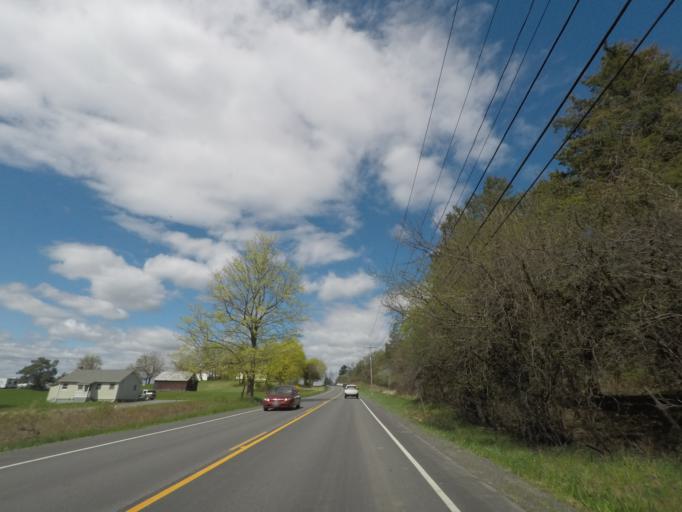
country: US
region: New York
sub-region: Columbia County
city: Oakdale
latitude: 42.2231
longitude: -73.7870
